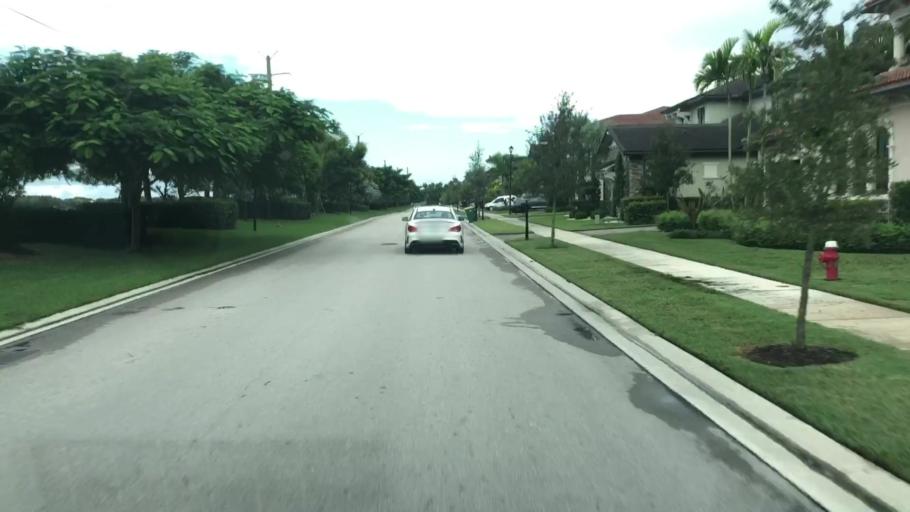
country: US
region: Florida
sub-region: Broward County
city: Parkland
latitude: 26.3398
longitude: -80.2755
